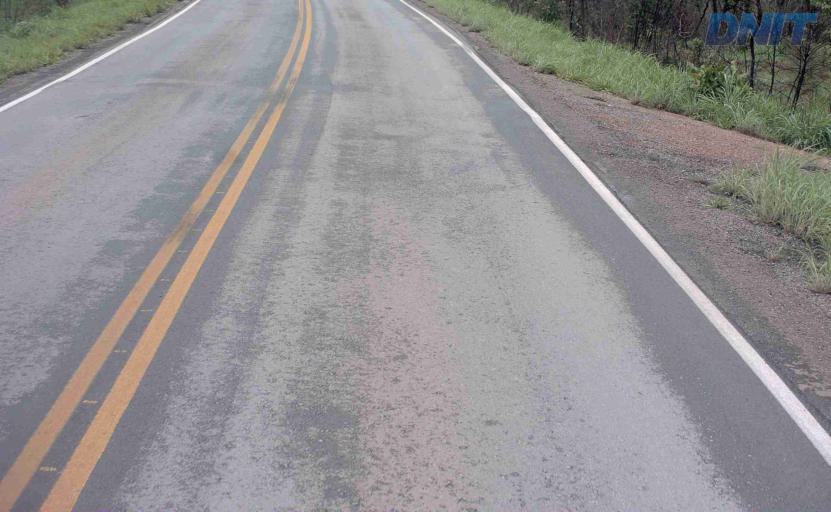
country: BR
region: Goias
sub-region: Padre Bernardo
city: Padre Bernardo
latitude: -15.4648
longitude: -48.2244
